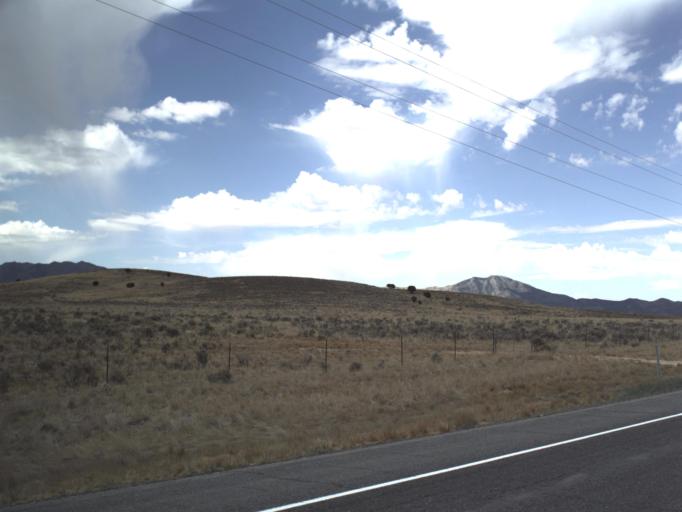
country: US
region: Utah
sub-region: Utah County
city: Eagle Mountain
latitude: 40.0763
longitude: -112.3890
